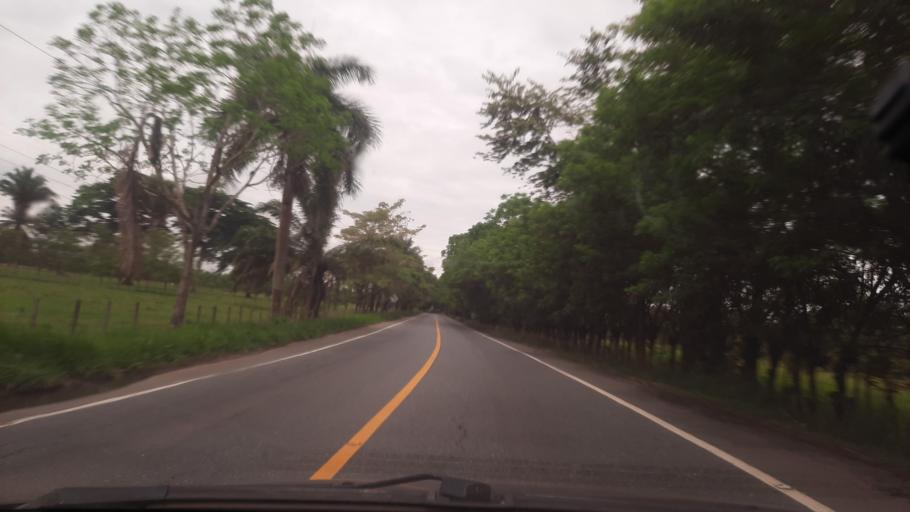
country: GT
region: Izabal
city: Morales
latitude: 15.4679
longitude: -88.9076
